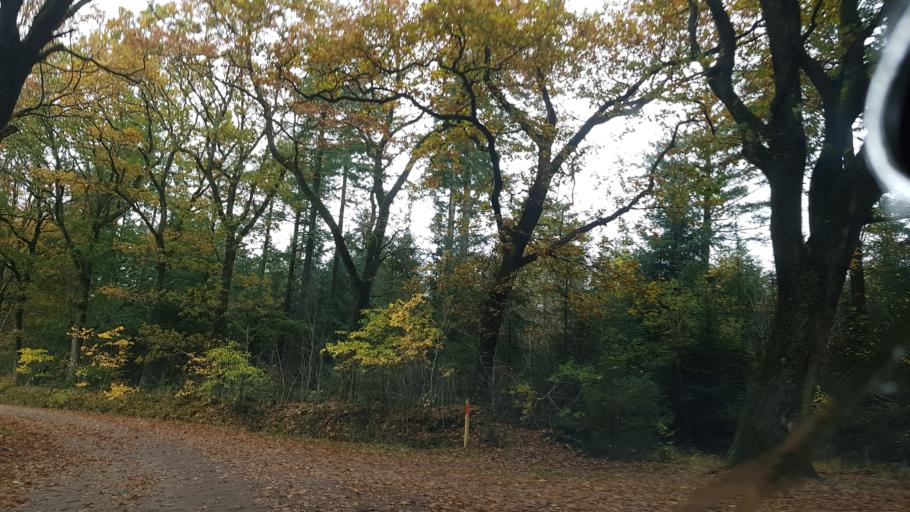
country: DK
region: South Denmark
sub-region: Tonder Kommune
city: Sherrebek
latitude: 55.1837
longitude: 8.7657
